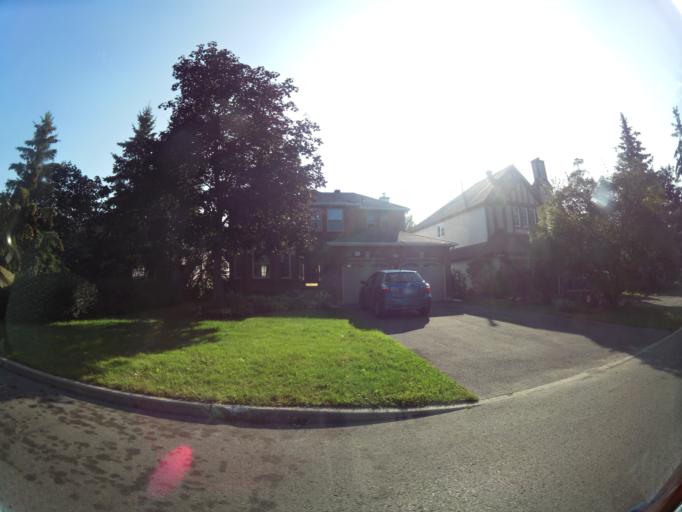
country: CA
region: Ontario
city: Clarence-Rockland
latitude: 45.4850
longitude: -75.4787
